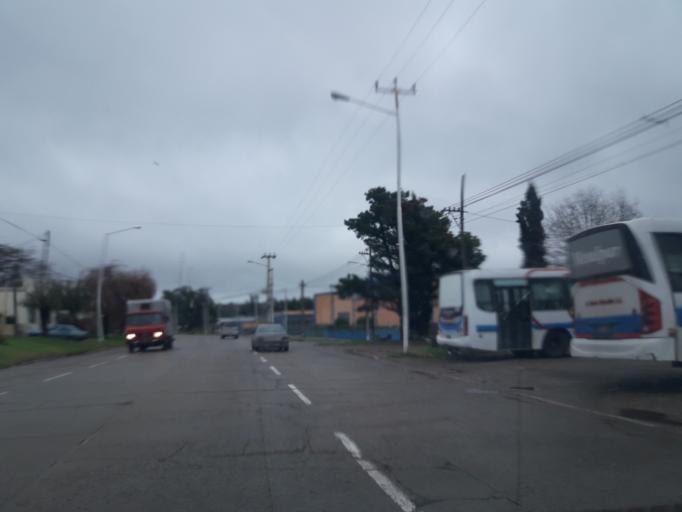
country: AR
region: Buenos Aires
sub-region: Partido de Tandil
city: Tandil
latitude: -37.3205
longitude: -59.1635
